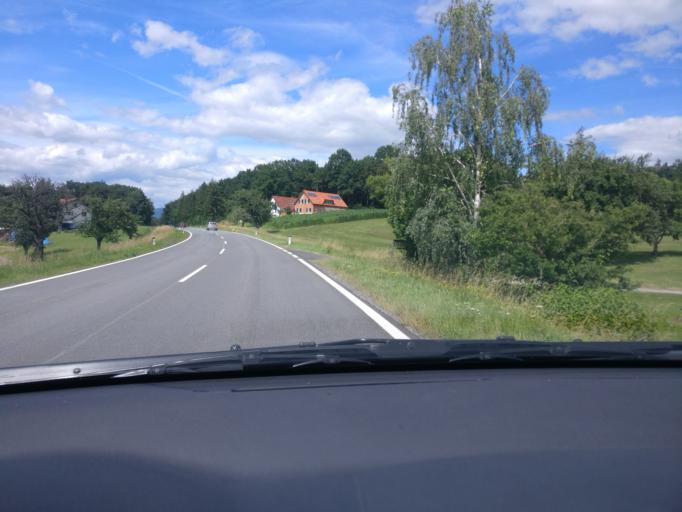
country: AT
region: Styria
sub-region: Politischer Bezirk Hartberg-Fuerstenfeld
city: Kaibing
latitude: 47.2073
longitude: 15.8536
